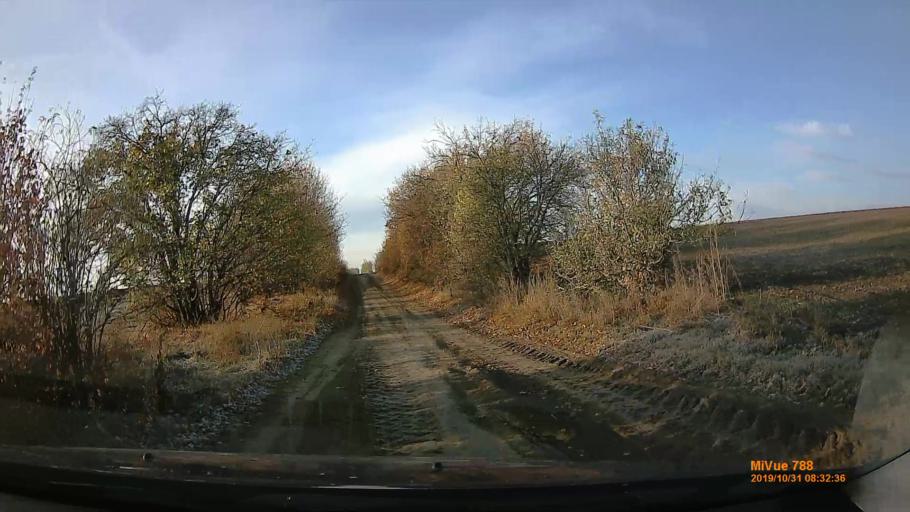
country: HU
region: Pest
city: Pand
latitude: 47.3425
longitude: 19.6625
